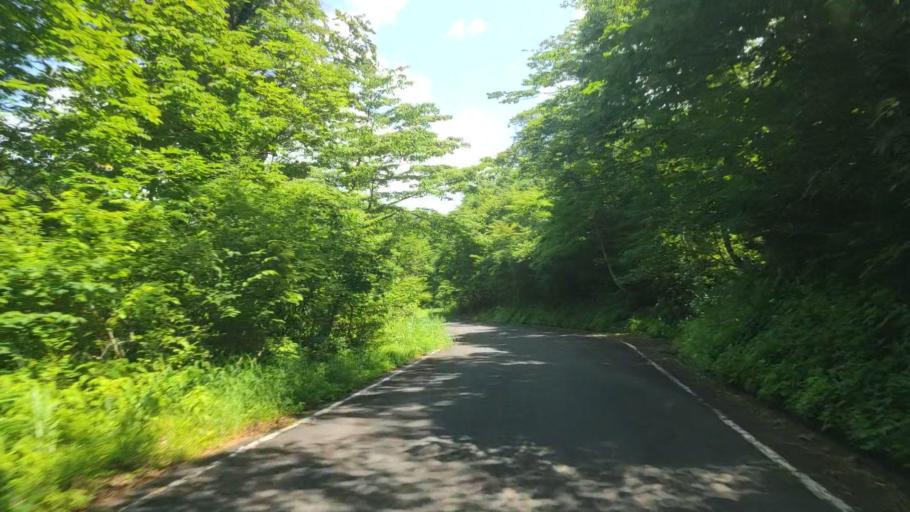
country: JP
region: Fukui
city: Ono
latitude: 35.7750
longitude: 136.5263
